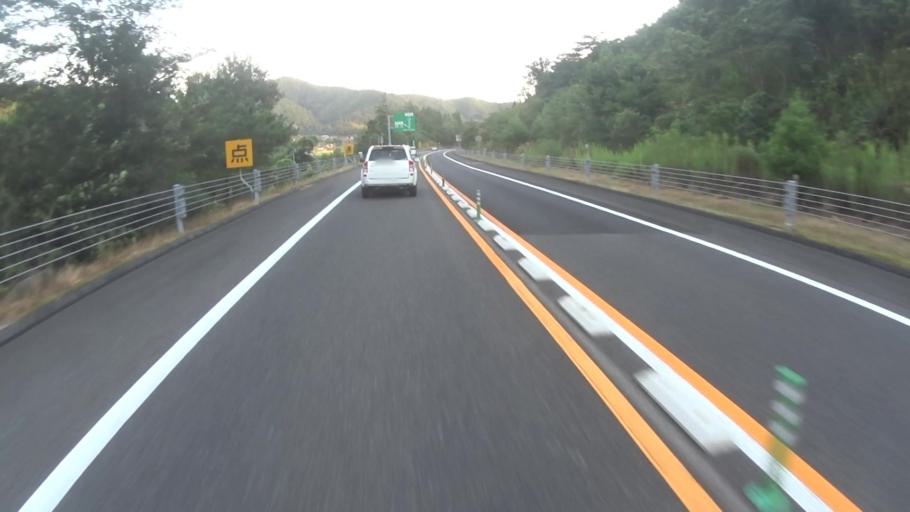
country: JP
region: Kyoto
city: Ayabe
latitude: 35.3638
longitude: 135.2878
